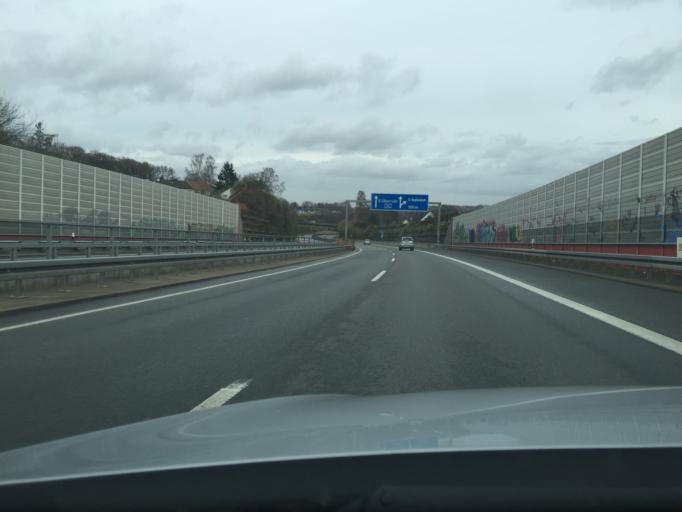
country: DE
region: North Rhine-Westphalia
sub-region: Regierungsbezirk Dusseldorf
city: Velbert
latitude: 51.3780
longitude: 7.0773
